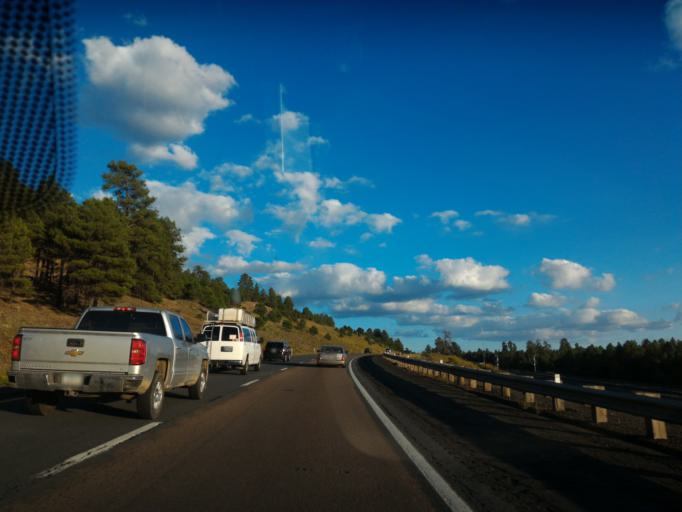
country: US
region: Arizona
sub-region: Coconino County
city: Flagstaff
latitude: 35.2108
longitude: -111.7735
